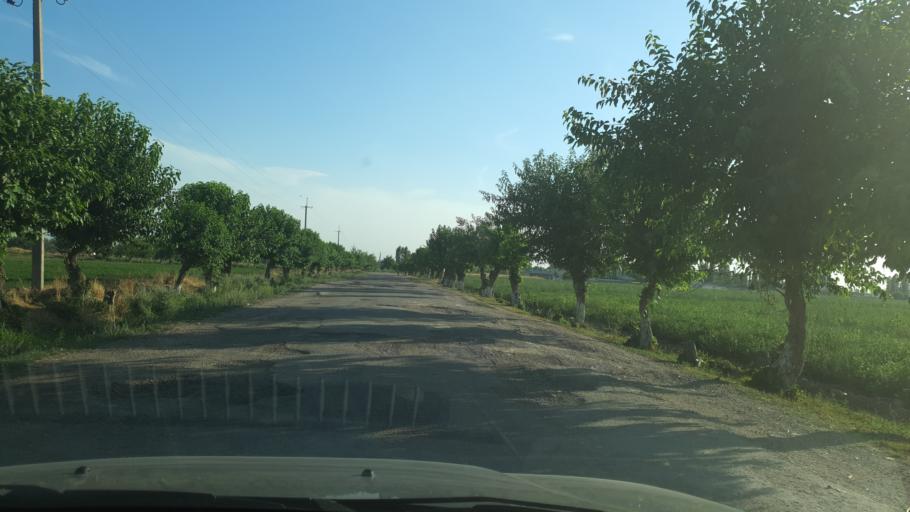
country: UZ
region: Toshkent
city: Tuytepa
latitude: 41.0925
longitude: 69.3701
